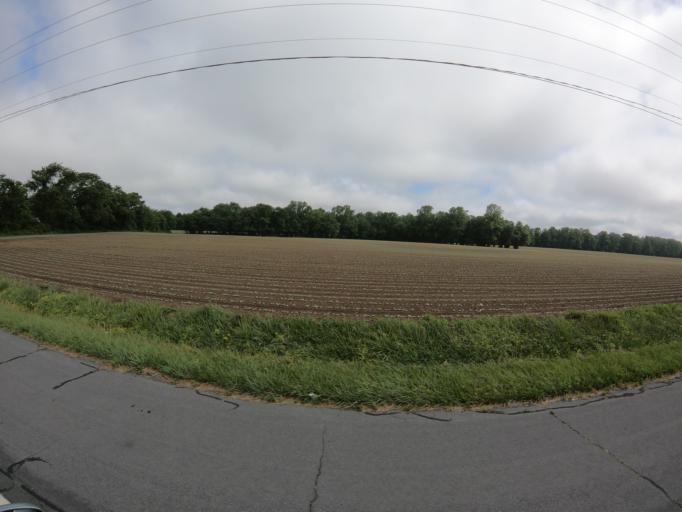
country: US
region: Delaware
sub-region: Kent County
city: Riverview
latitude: 39.0054
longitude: -75.5368
